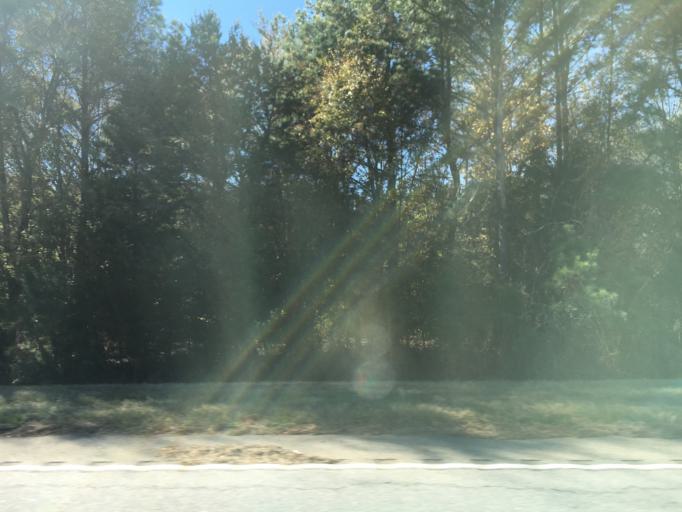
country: US
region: South Carolina
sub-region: Spartanburg County
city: Roebuck
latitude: 34.8718
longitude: -82.0348
